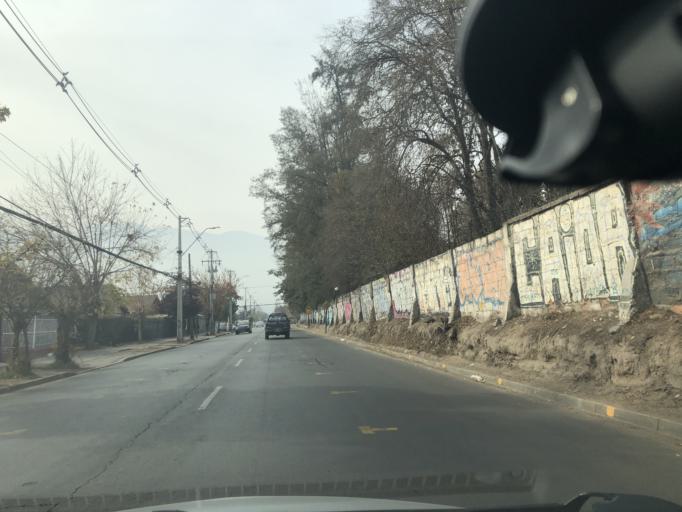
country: CL
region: Santiago Metropolitan
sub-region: Provincia de Cordillera
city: Puente Alto
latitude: -33.5689
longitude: -70.5796
